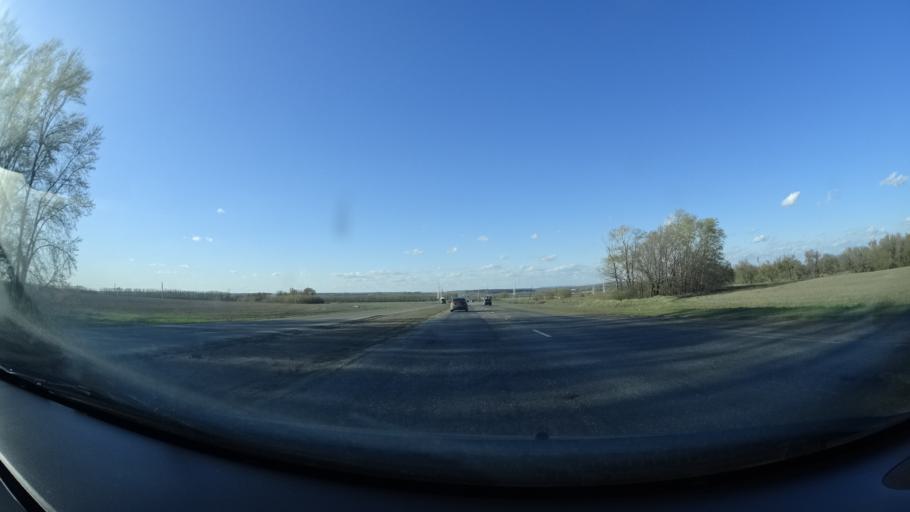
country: RU
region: Bashkortostan
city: Kabakovo
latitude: 54.4730
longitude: 55.9119
